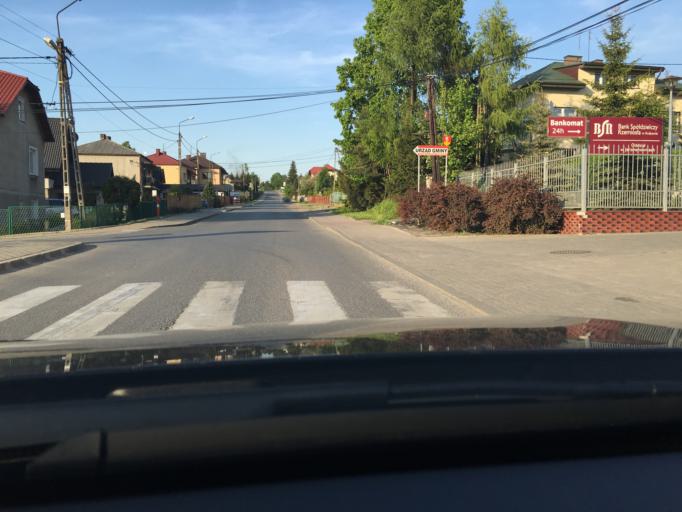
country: PL
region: Lesser Poland Voivodeship
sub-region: Powiat krakowski
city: Jerzmanowice
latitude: 50.2129
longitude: 19.7486
